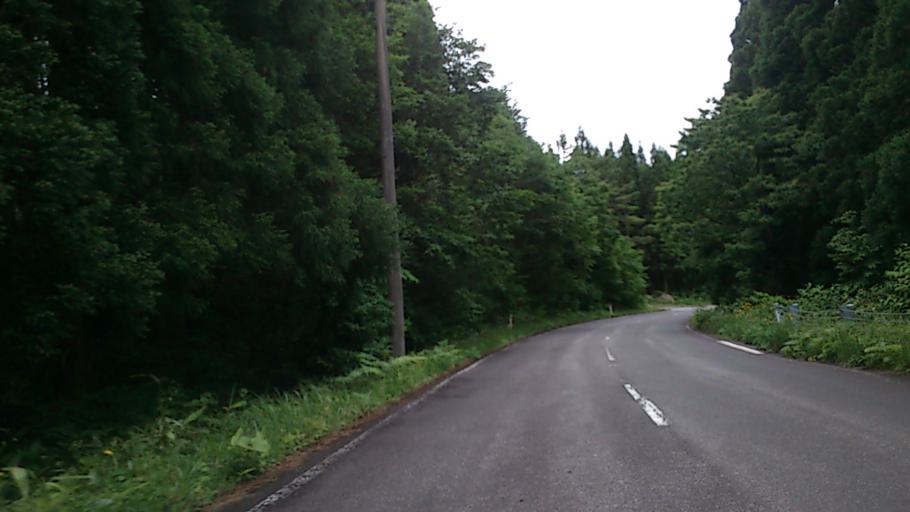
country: JP
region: Yamagata
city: Yuza
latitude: 39.1017
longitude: 139.9414
